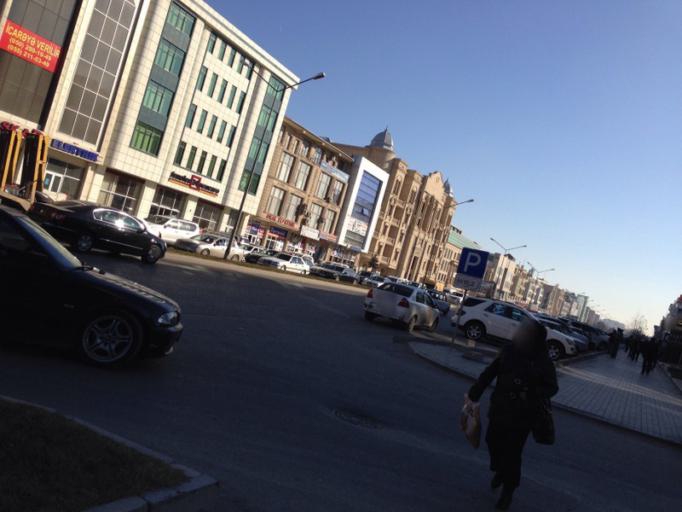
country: AZ
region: Baki
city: Baku
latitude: 40.4136
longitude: 49.8602
